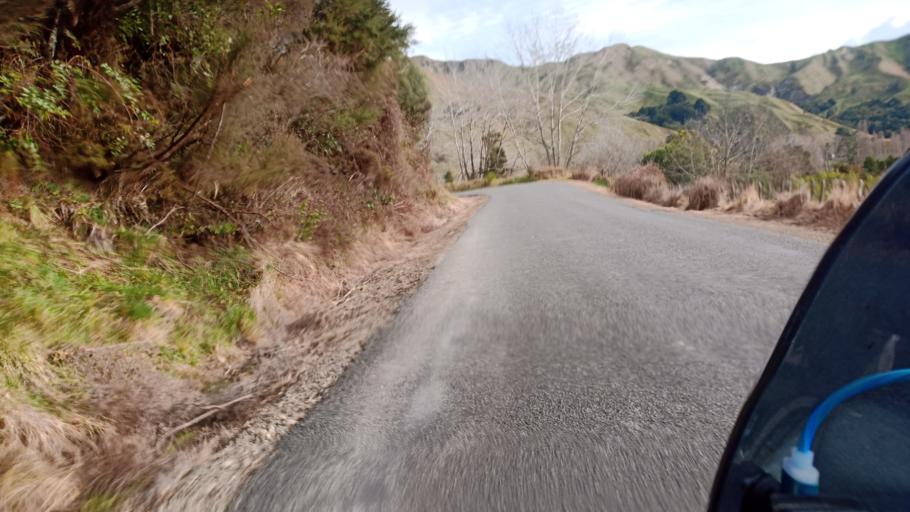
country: NZ
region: Hawke's Bay
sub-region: Wairoa District
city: Wairoa
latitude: -38.7959
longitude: 177.4425
